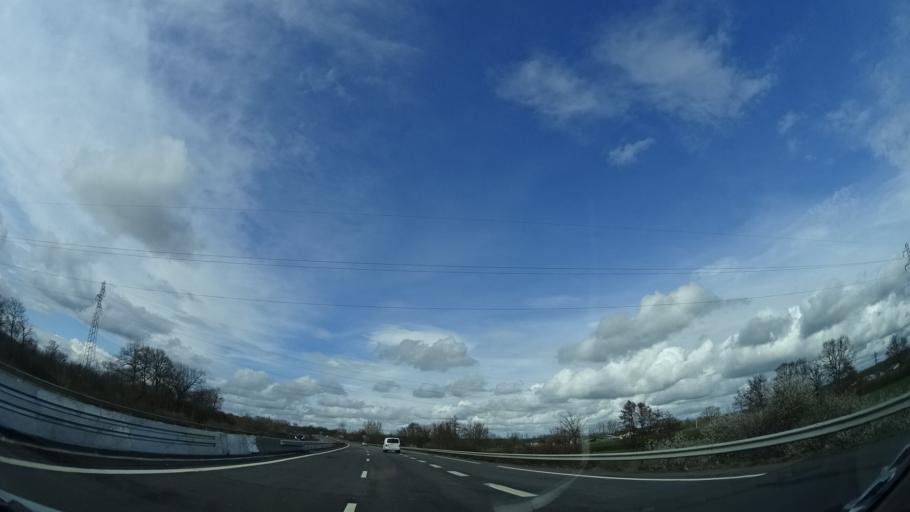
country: FR
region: Rhone-Alpes
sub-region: Departement de la Loire
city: Le Coteau
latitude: 46.0362
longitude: 4.1000
